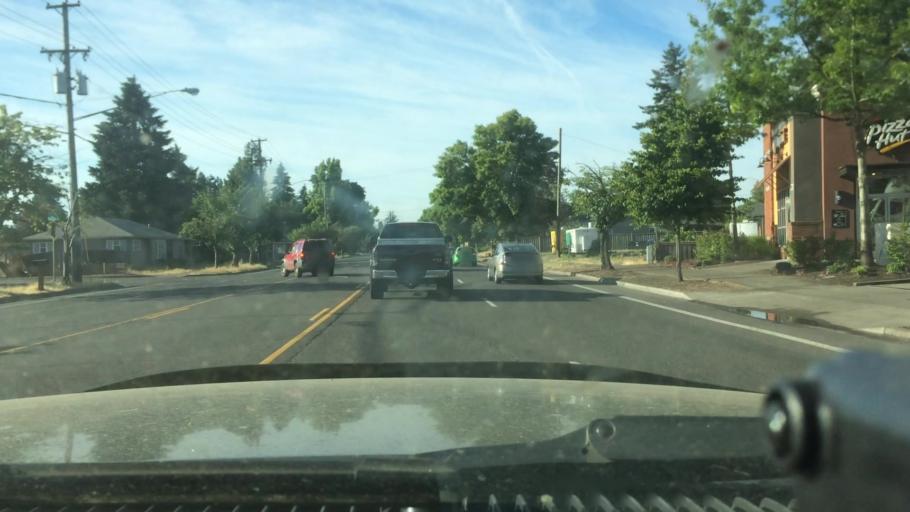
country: US
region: Oregon
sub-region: Lane County
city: Eugene
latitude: 44.0937
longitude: -123.1273
